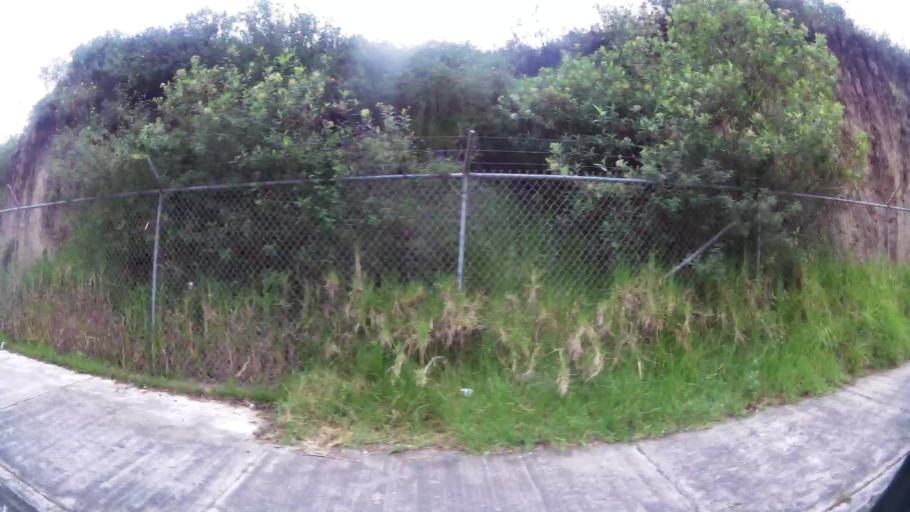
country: EC
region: Pichincha
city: Quito
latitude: -0.1587
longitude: -78.4976
